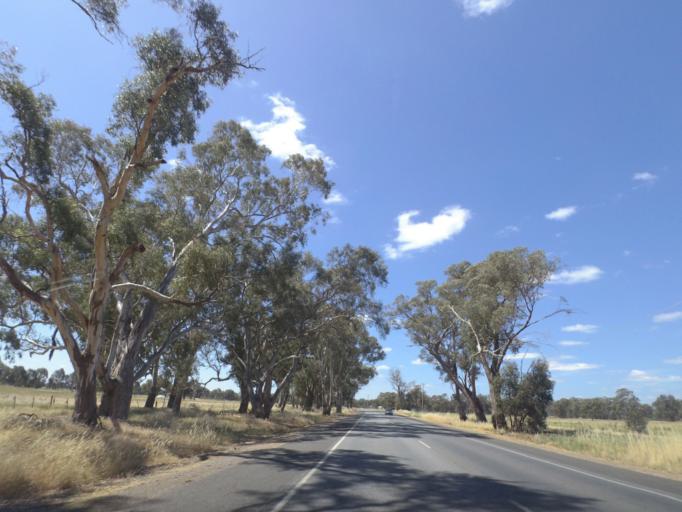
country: AU
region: Victoria
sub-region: Wangaratta
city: Wangaratta
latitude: -36.4008
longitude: 146.2769
